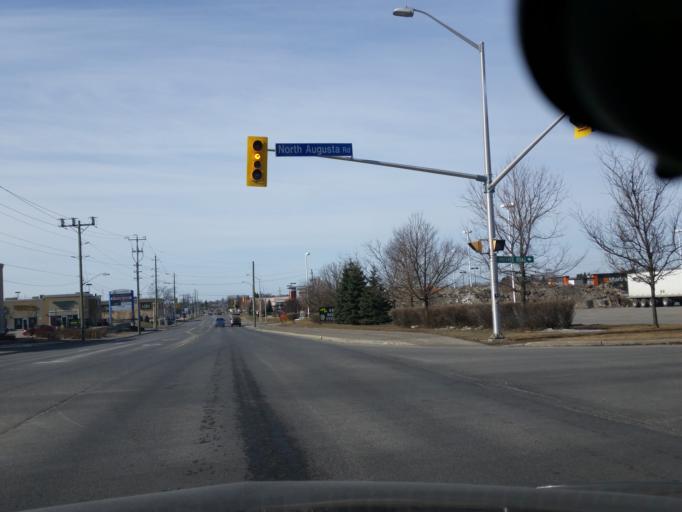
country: CA
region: Ontario
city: Brockville
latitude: 44.6133
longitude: -75.6864
